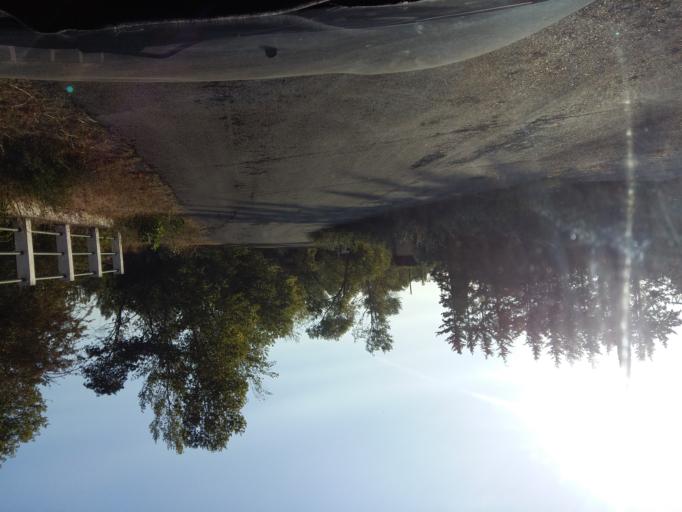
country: FR
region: Provence-Alpes-Cote d'Azur
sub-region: Departement du Vaucluse
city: Loriol-du-Comtat
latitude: 44.0797
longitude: 4.9892
